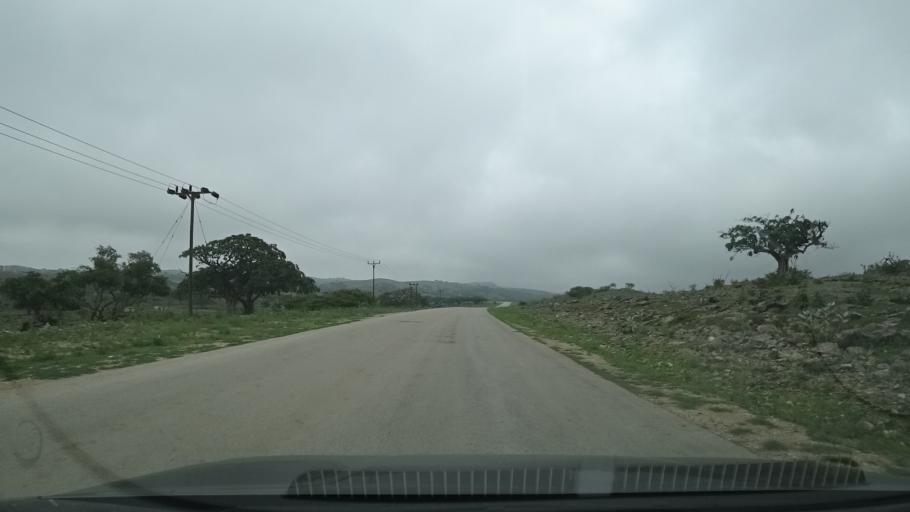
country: OM
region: Zufar
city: Salalah
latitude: 17.1193
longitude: 54.5682
